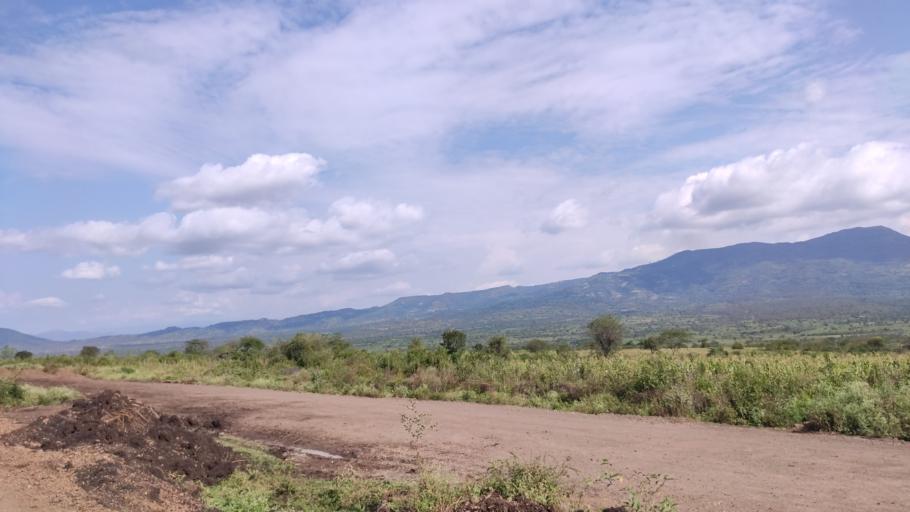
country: ET
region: Southern Nations, Nationalities, and People's Region
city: Felege Neway
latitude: 6.3956
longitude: 37.1058
